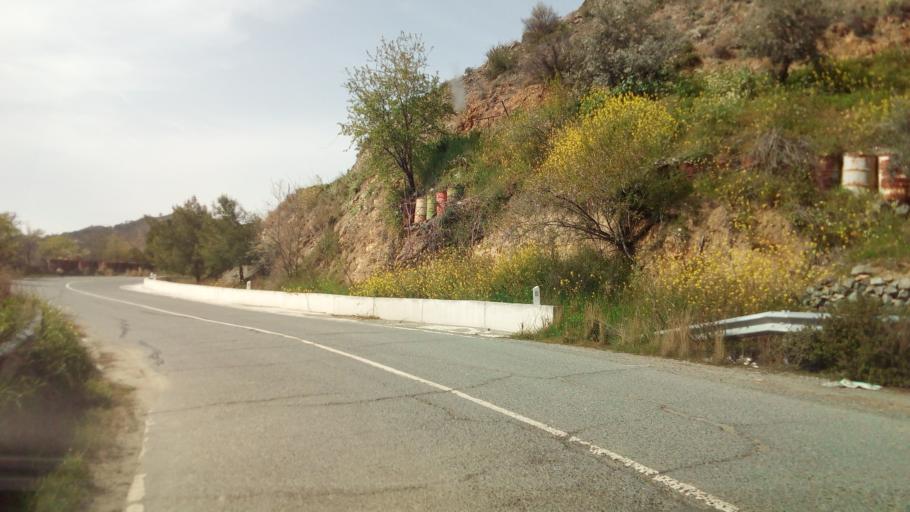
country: CY
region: Limassol
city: Pelendri
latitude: 34.8931
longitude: 32.9717
